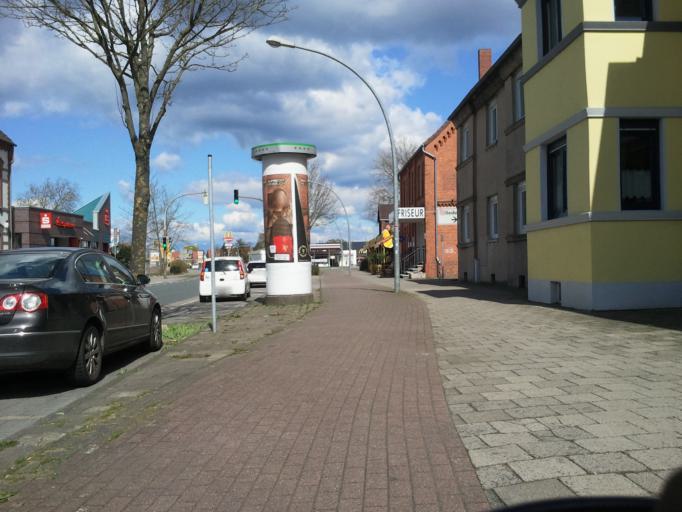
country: DE
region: Lower Saxony
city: Nienburg
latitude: 52.6510
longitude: 9.2167
